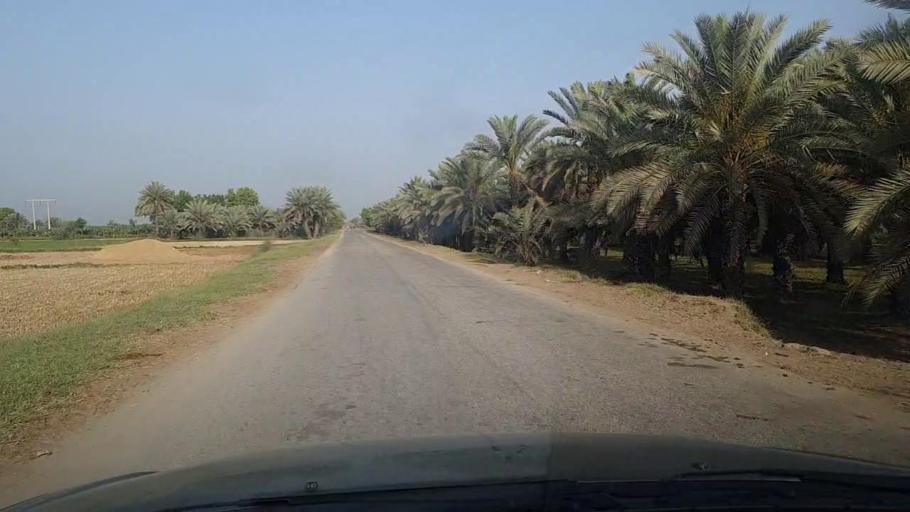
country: PK
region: Sindh
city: Pir jo Goth
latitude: 27.5640
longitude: 68.6509
